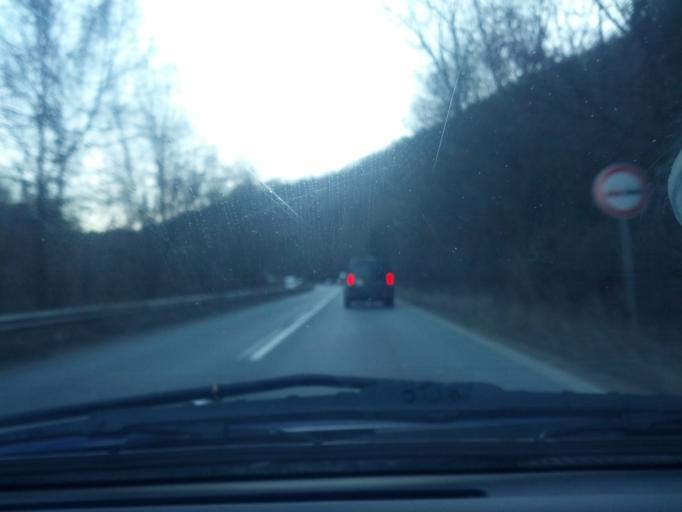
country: BG
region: Vratsa
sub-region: Obshtina Mezdra
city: Mezdra
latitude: 43.0777
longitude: 23.6810
